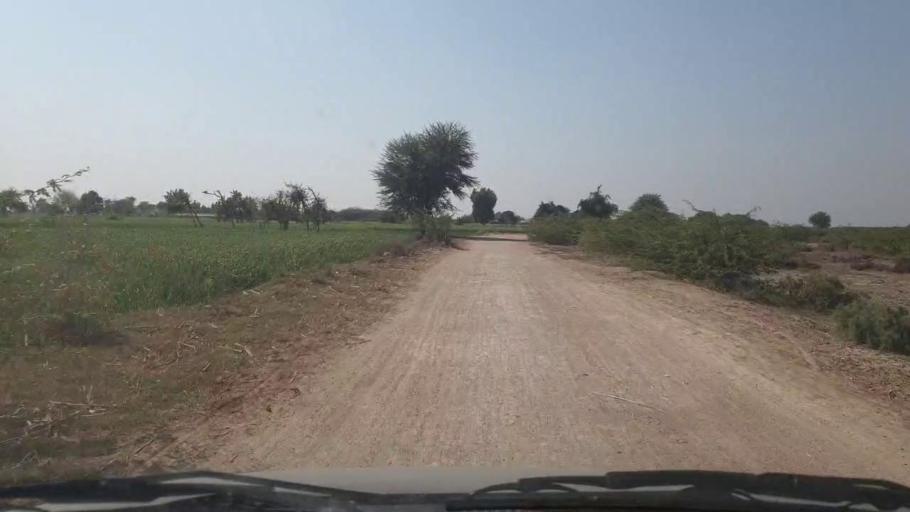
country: PK
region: Sindh
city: Samaro
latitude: 25.2616
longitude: 69.3377
